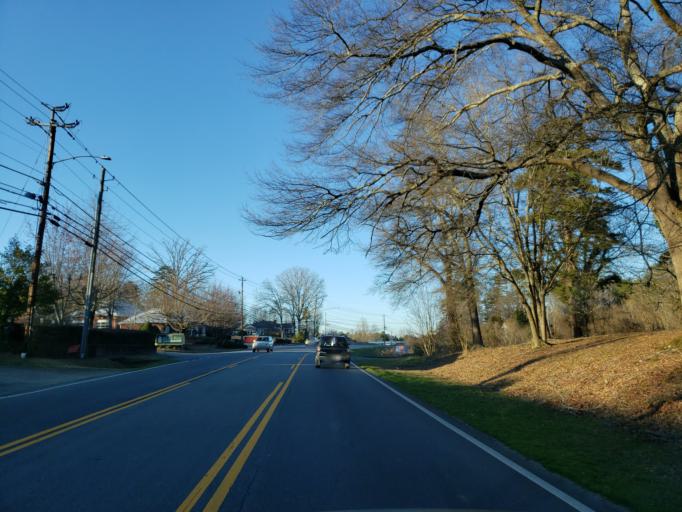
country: US
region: Georgia
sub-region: Cherokee County
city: Canton
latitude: 34.2074
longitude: -84.5059
